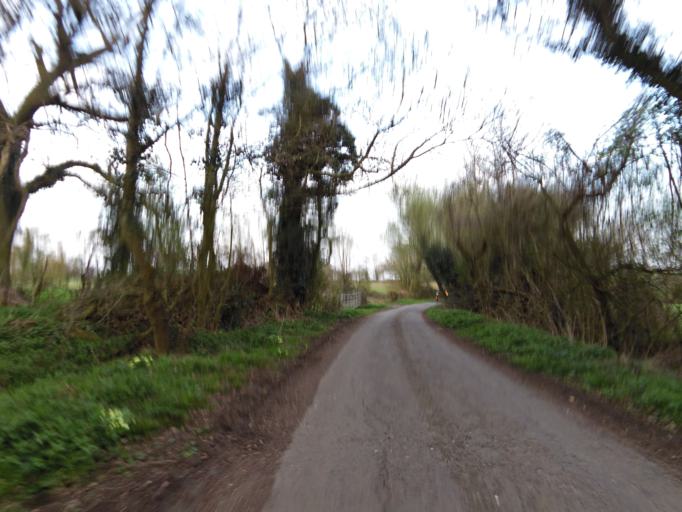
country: GB
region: England
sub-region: Suffolk
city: Kesgrave
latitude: 52.1487
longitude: 1.2354
